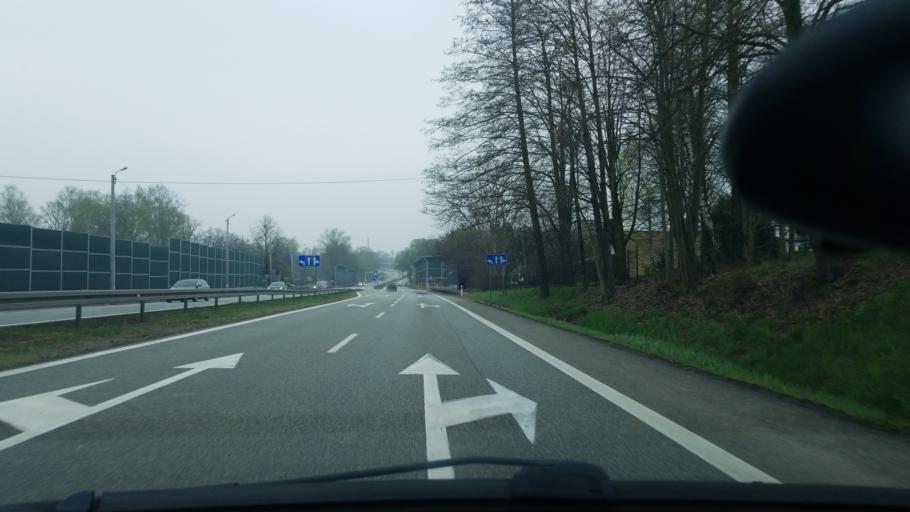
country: PL
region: Silesian Voivodeship
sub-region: Powiat pszczynski
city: Pawlowice
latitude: 49.9976
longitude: 18.7114
